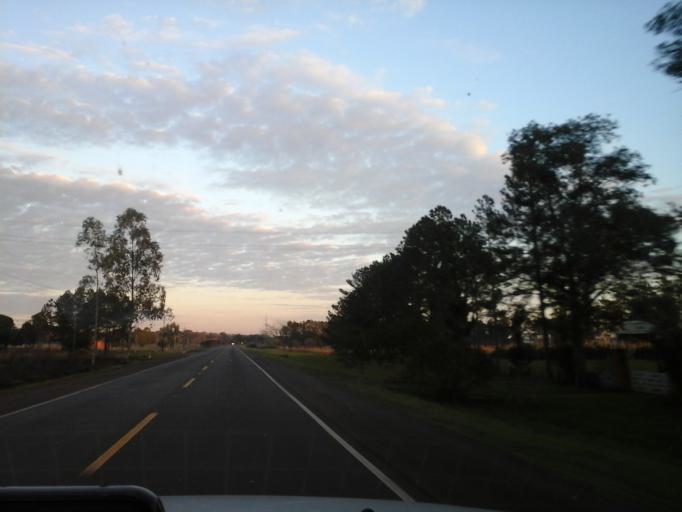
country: PY
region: Itapua
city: General Delgado
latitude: -27.0733
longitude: -56.5985
